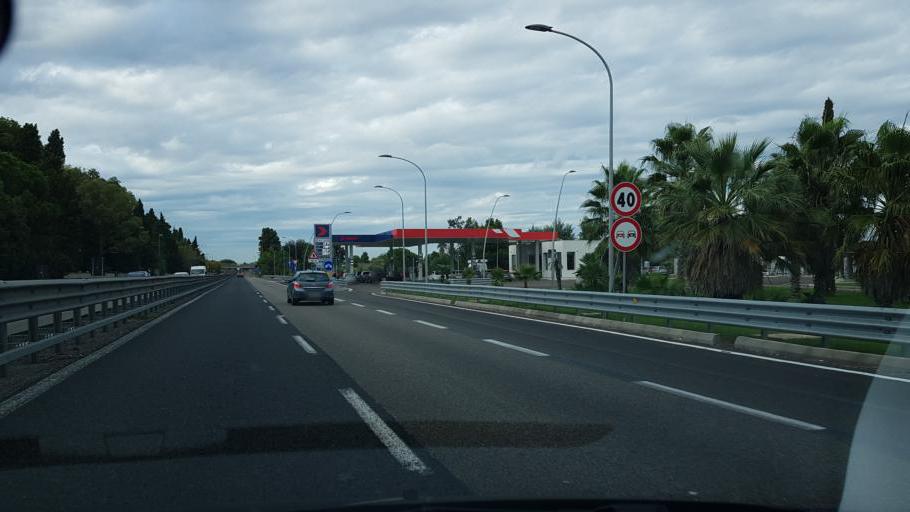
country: IT
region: Apulia
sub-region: Provincia di Lecce
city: Cavallino
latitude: 40.3034
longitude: 18.1923
